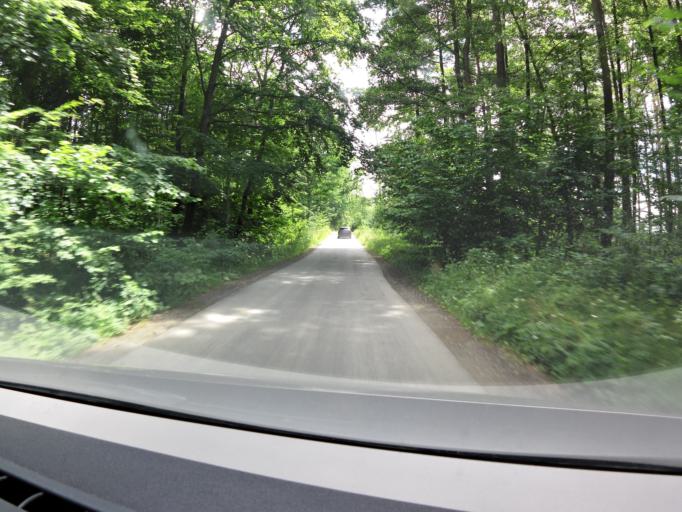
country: DE
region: Baden-Wuerttemberg
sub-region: Tuebingen Region
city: Tuebingen
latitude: 48.5509
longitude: 9.0024
